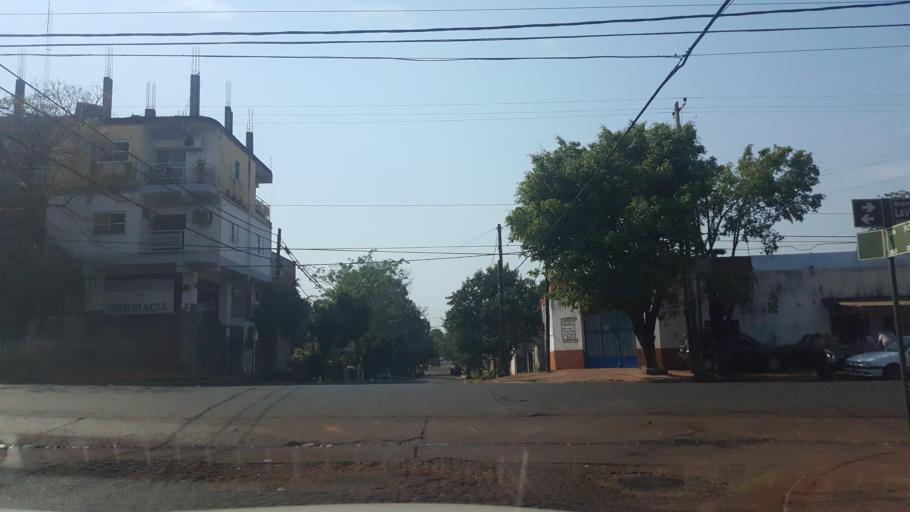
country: AR
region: Misiones
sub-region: Departamento de Capital
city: Posadas
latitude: -27.4019
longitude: -55.9102
